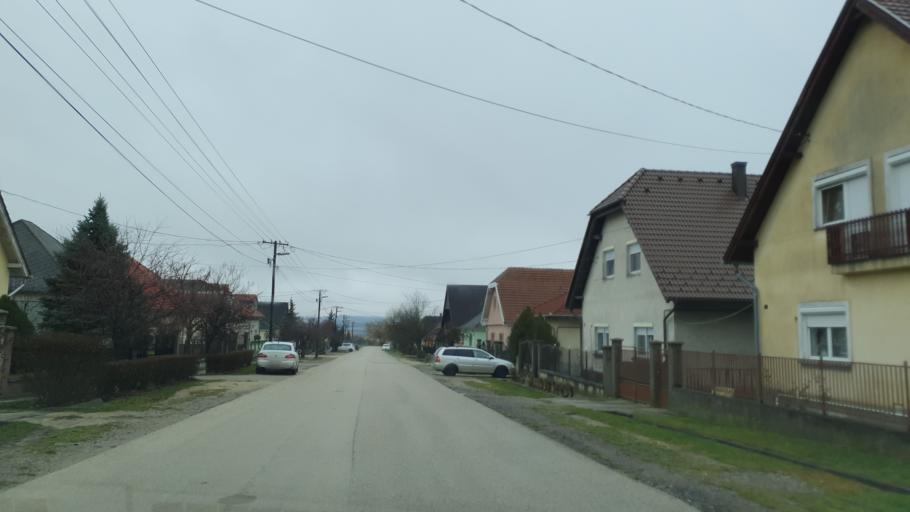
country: HU
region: Veszprem
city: Hajmasker
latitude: 47.1454
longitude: 17.9552
